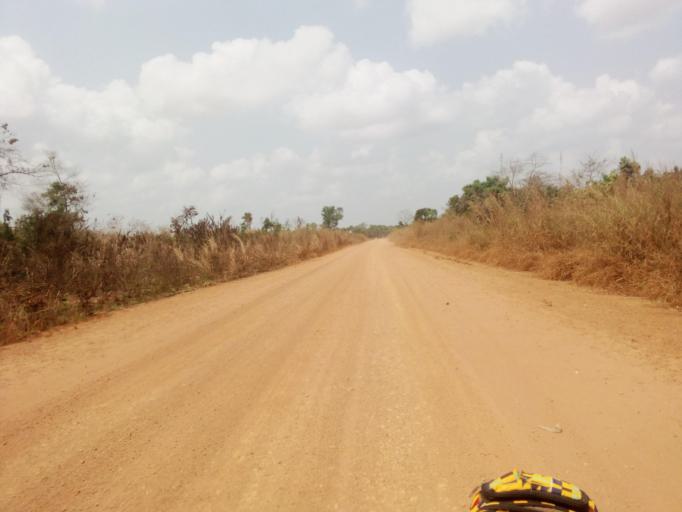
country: SL
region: Southern Province
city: Mogbwemo
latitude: 7.6628
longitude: -12.2707
